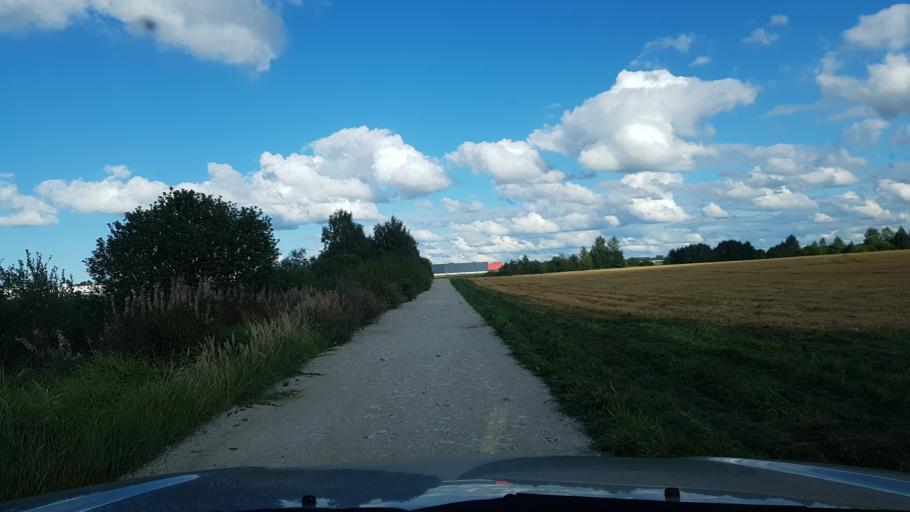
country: EE
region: Harju
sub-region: Rae vald
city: Jueri
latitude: 59.3568
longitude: 24.8500
